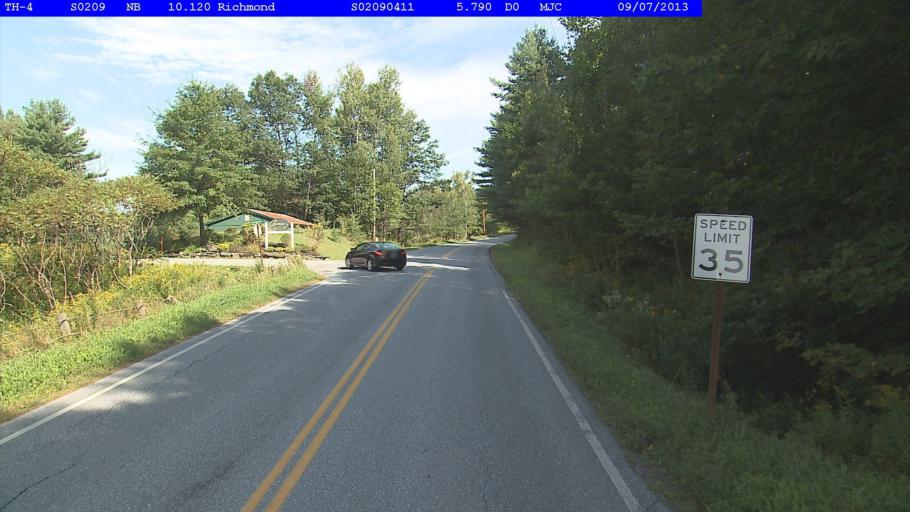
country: US
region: Vermont
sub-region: Chittenden County
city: Williston
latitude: 44.4132
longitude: -72.9907
